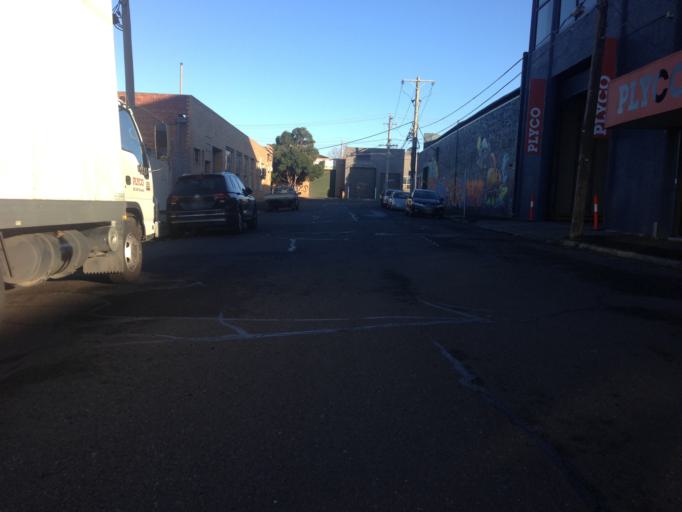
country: AU
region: Victoria
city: Alphington
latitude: -37.7697
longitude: 145.0288
